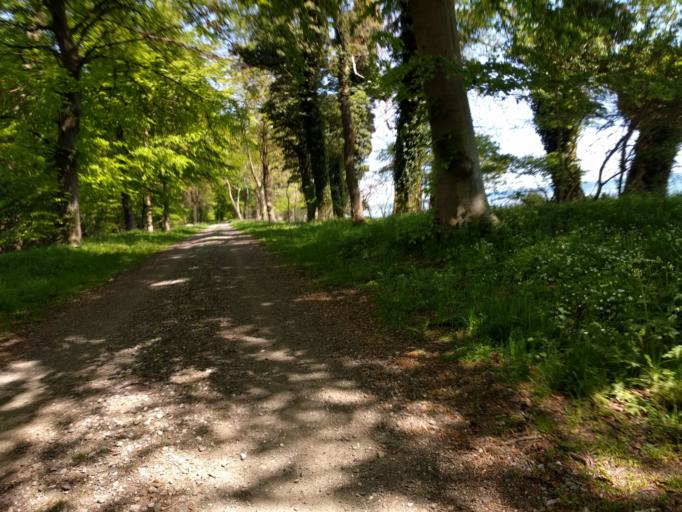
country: DK
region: Zealand
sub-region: Guldborgsund Kommune
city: Stubbekobing
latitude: 54.7898
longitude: 12.0823
